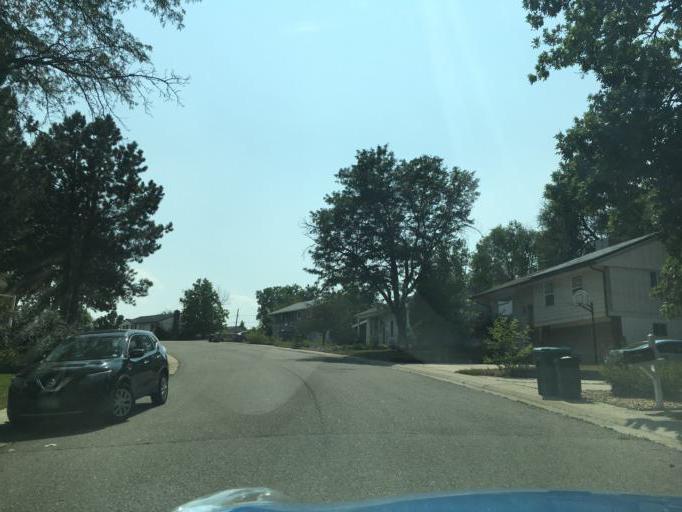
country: US
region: Colorado
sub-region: Adams County
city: Westminster
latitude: 39.8379
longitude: -105.0743
